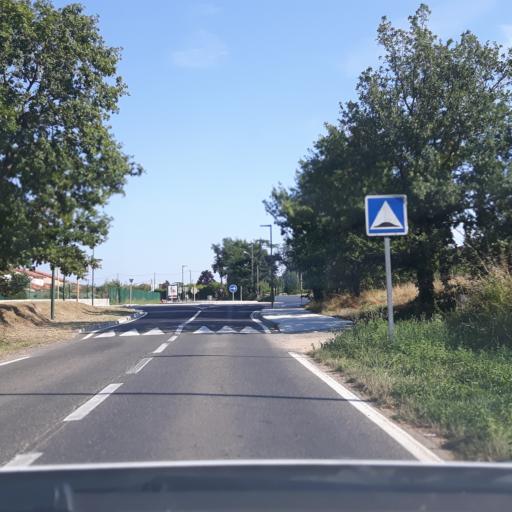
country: FR
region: Midi-Pyrenees
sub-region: Departement de la Haute-Garonne
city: Fronton
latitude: 43.8366
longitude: 1.3953
